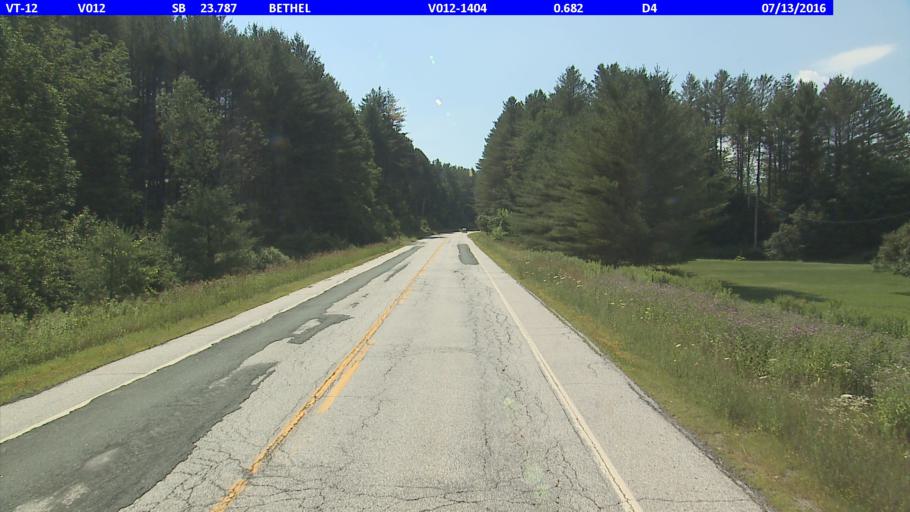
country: US
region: Vermont
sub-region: Orange County
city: Randolph
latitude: 43.8002
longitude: -72.6520
